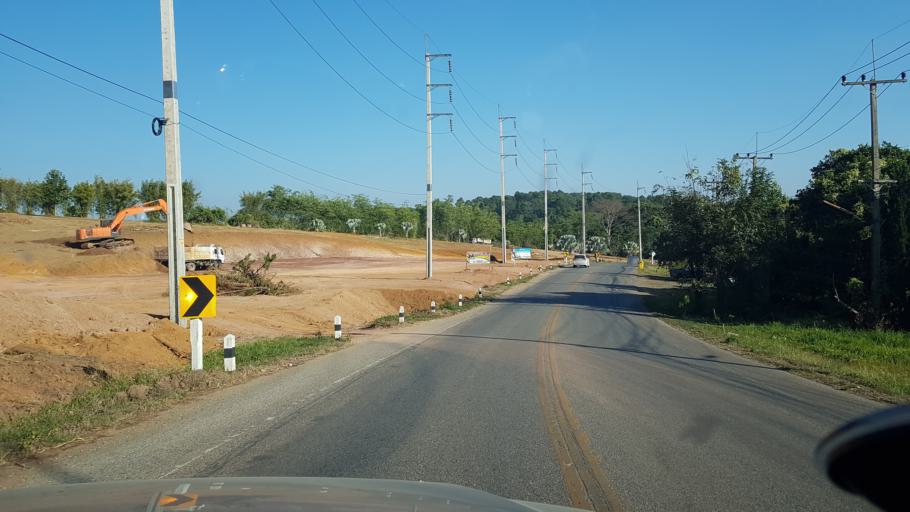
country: TH
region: Phetchabun
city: Khao Kho
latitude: 16.7148
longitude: 101.0333
